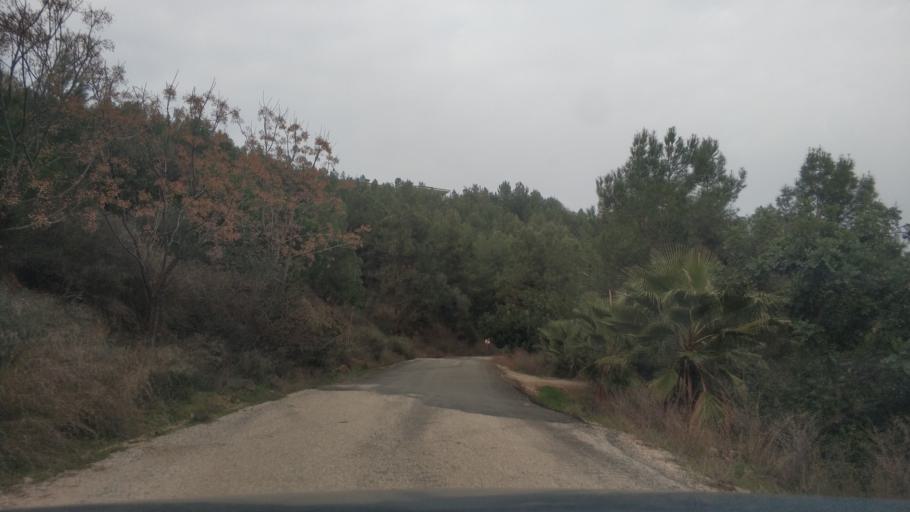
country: TR
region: Adana
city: Adana
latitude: 37.0779
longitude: 35.3260
